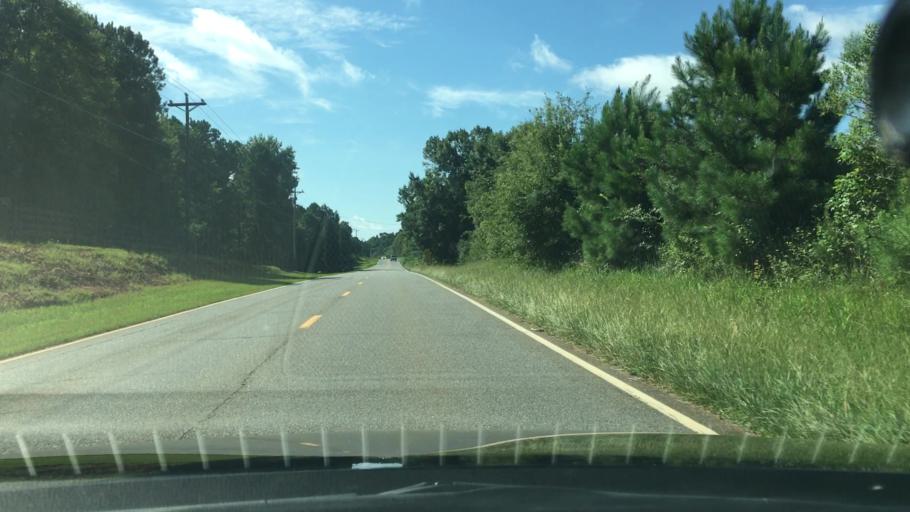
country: US
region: Georgia
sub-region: Putnam County
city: Jefferson
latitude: 33.4485
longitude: -83.2961
